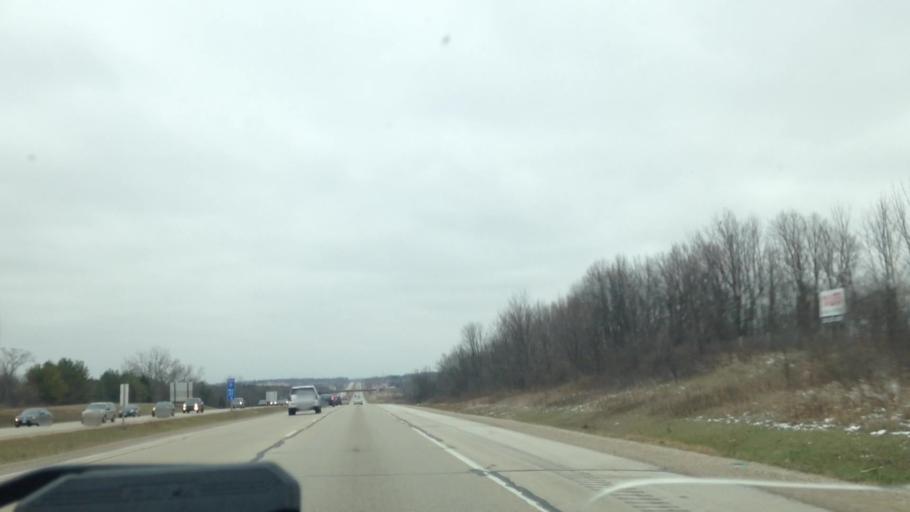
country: US
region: Wisconsin
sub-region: Washington County
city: Slinger
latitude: 43.3170
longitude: -88.2409
